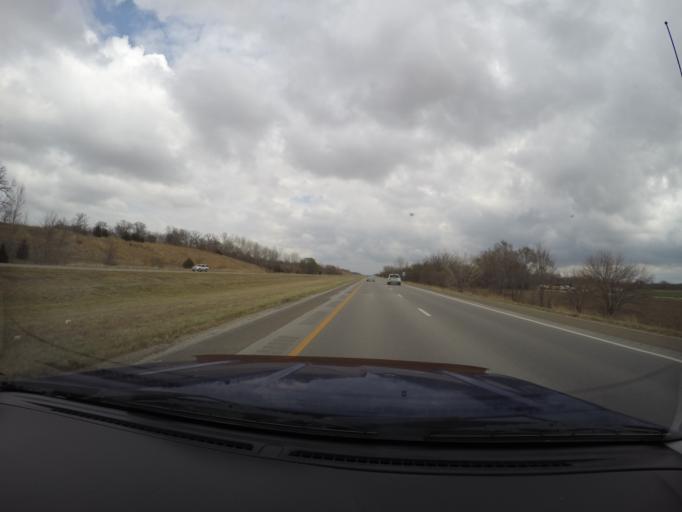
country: US
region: Kansas
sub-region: Riley County
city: Manhattan
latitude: 39.1973
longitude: -96.4812
